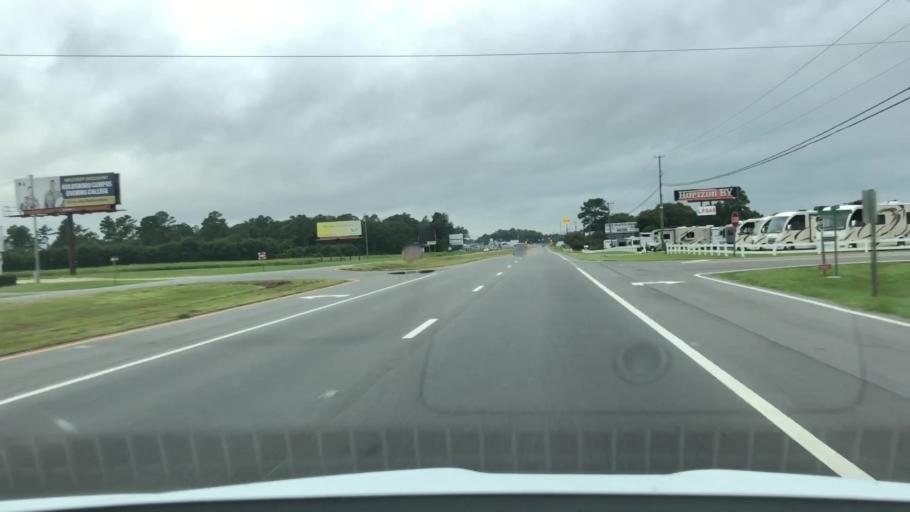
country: US
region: North Carolina
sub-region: Lenoir County
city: La Grange
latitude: 35.2817
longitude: -77.7521
